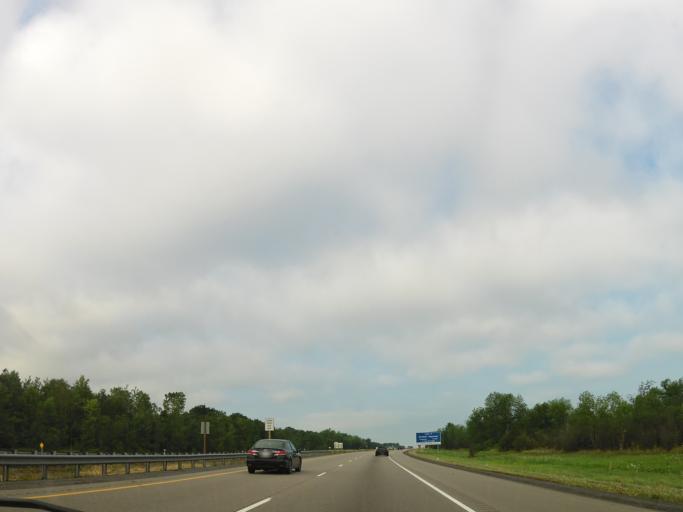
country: CA
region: Ontario
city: Skatepark
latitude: 44.2734
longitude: -76.8906
